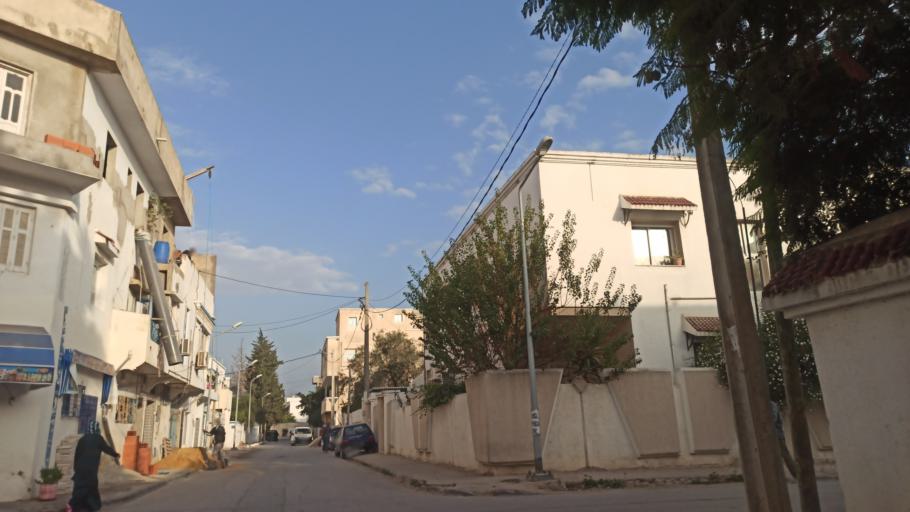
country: TN
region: Tunis
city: La Goulette
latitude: 36.8534
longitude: 10.2646
